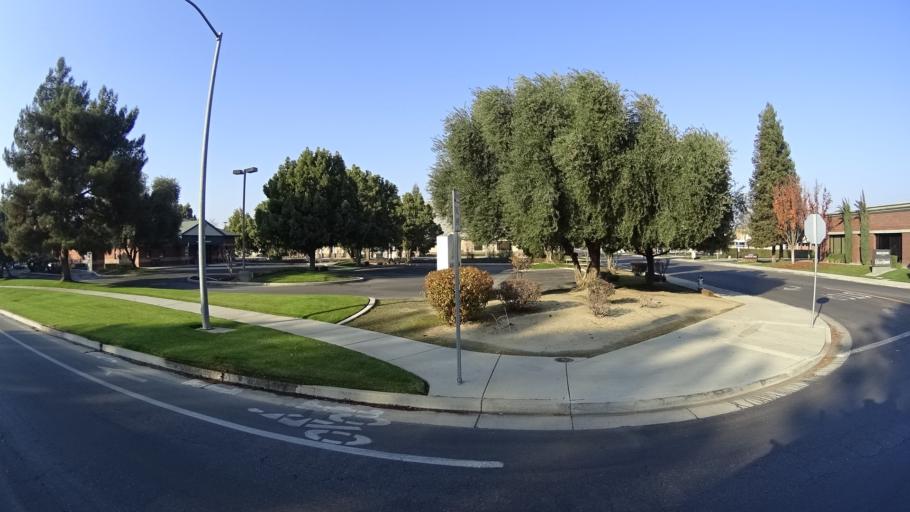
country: US
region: California
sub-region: Kern County
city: Greenacres
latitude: 35.3398
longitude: -119.0982
